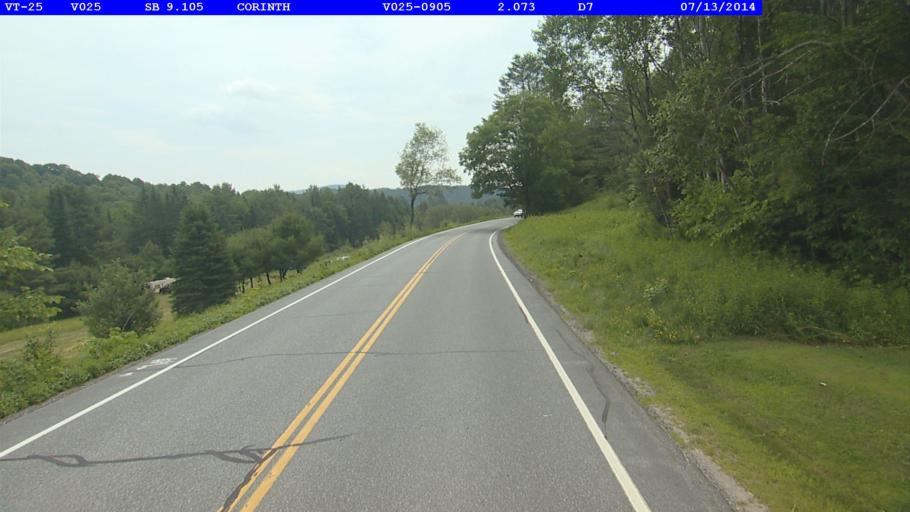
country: US
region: New Hampshire
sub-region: Grafton County
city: Haverhill
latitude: 44.0605
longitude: -72.2331
